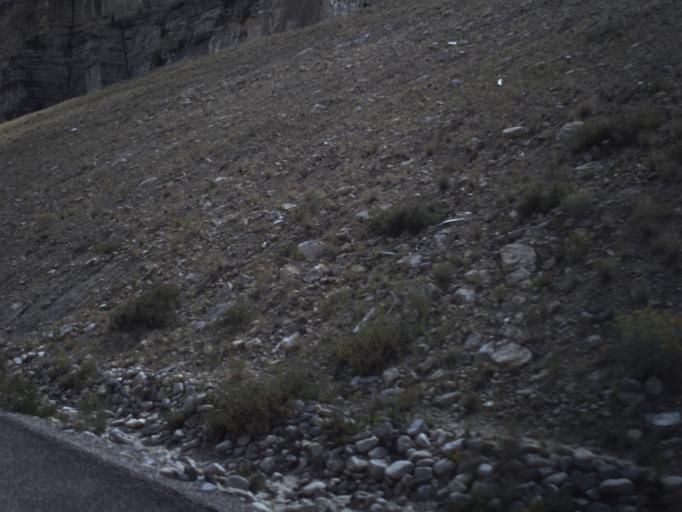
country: US
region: Utah
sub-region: Iron County
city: Cedar City
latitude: 37.6327
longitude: -112.9422
